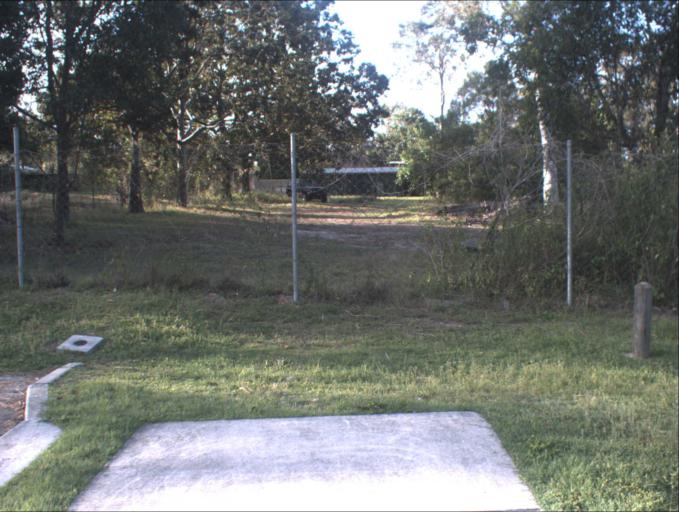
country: AU
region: Queensland
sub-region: Logan
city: Logan City
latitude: -27.6755
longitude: 153.0872
